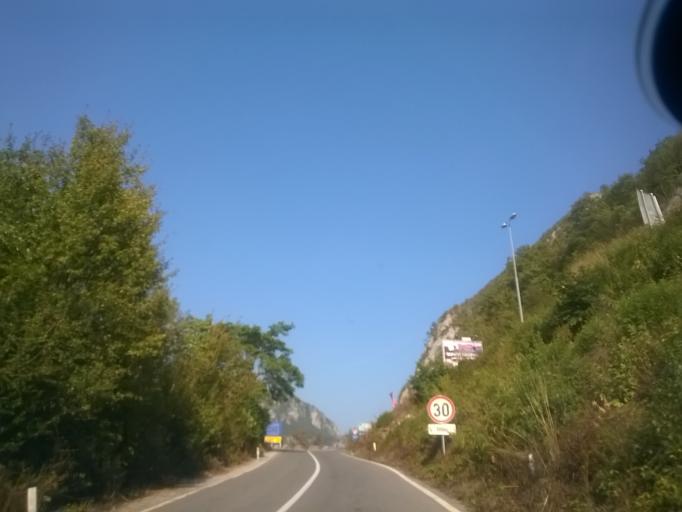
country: BA
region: Republika Srpska
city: Foca
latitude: 43.3486
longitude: 18.8478
